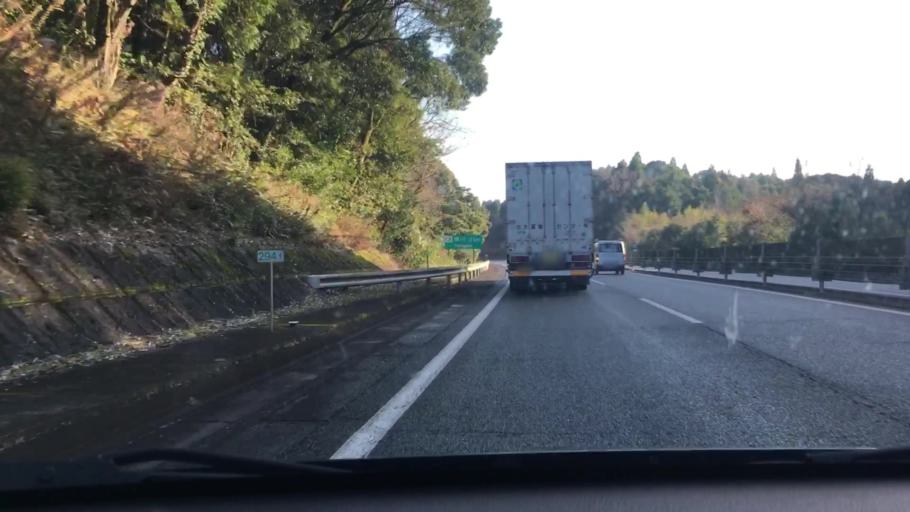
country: JP
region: Kagoshima
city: Okuchi-shinohara
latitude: 31.9144
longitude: 130.7036
